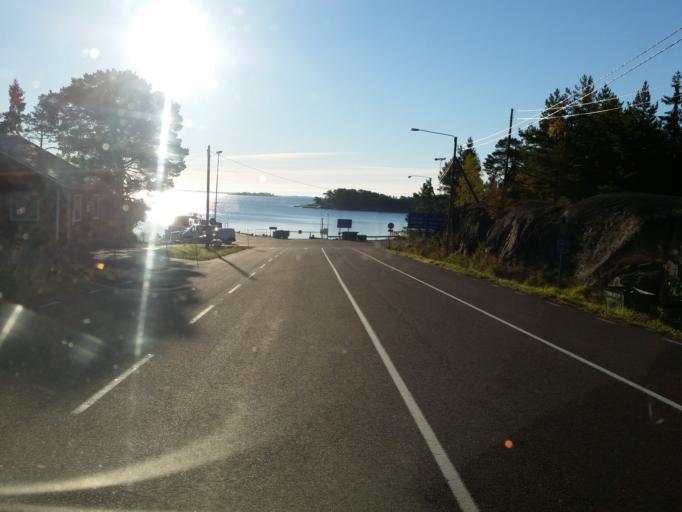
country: AX
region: Alands skaergard
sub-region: Vardoe
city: Vardoe
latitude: 60.2251
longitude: 20.4121
